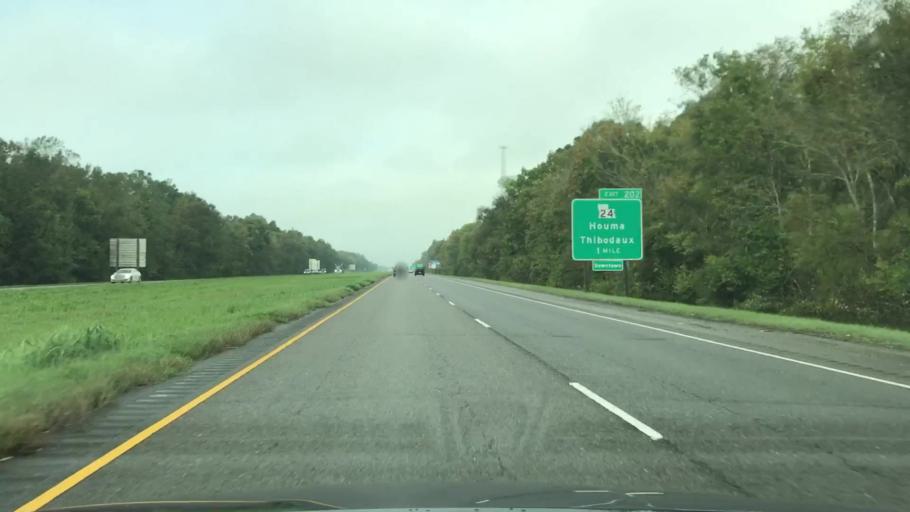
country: US
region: Louisiana
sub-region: Terrebonne Parish
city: Gray
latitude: 29.6817
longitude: -90.7619
